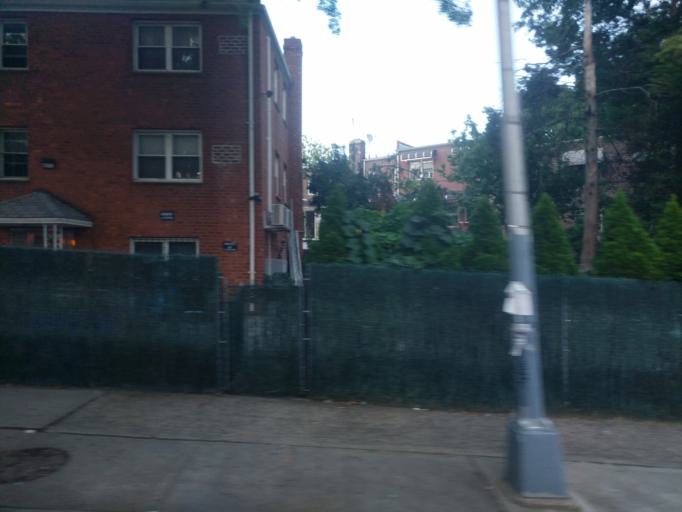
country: US
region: New York
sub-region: Queens County
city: Jamaica
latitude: 40.7405
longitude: -73.8249
